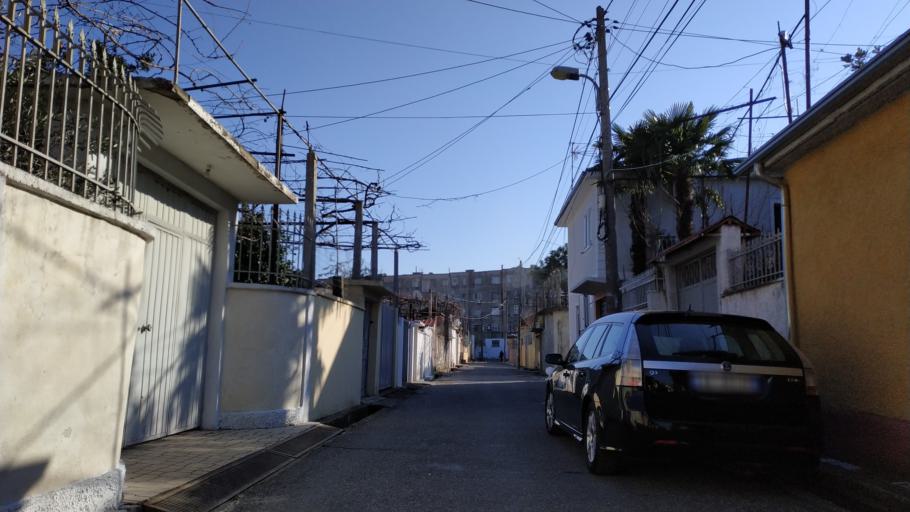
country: AL
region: Shkoder
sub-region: Rrethi i Shkodres
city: Shkoder
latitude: 42.0628
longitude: 19.5228
